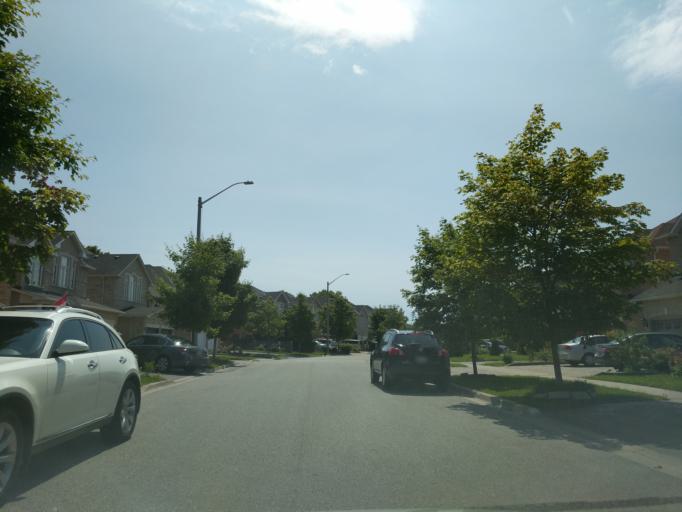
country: CA
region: Ontario
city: Markham
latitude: 43.8463
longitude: -79.2448
